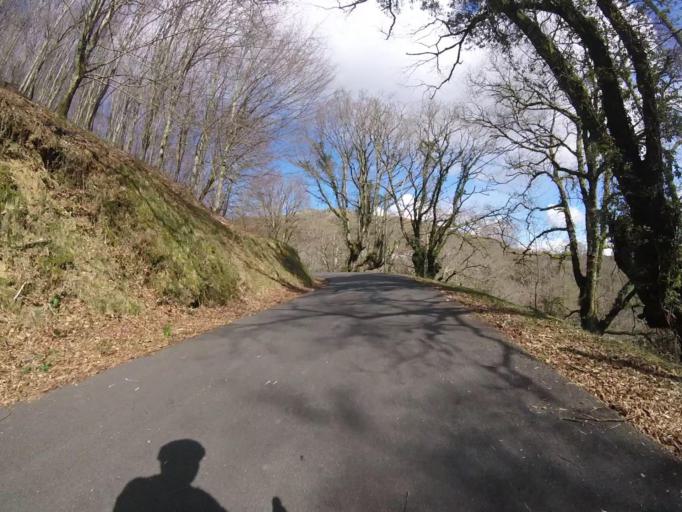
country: ES
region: Navarre
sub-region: Provincia de Navarra
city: Etxalar
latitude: 43.2613
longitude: -1.6175
